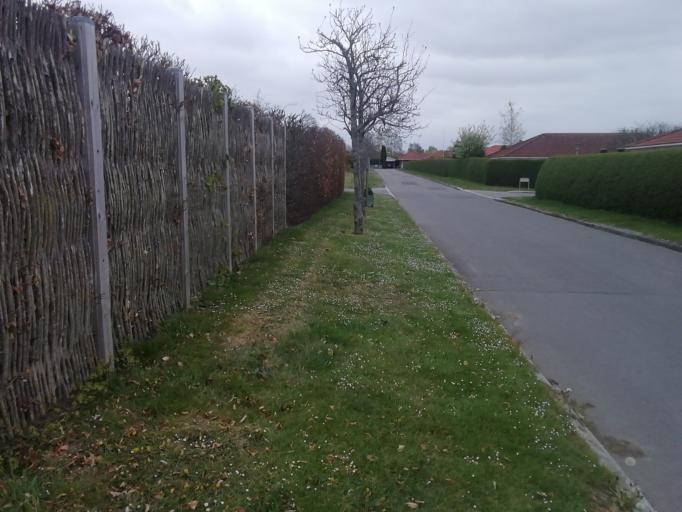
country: DK
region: Capital Region
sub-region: Egedal Kommune
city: Olstykke
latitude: 55.7709
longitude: 12.1585
